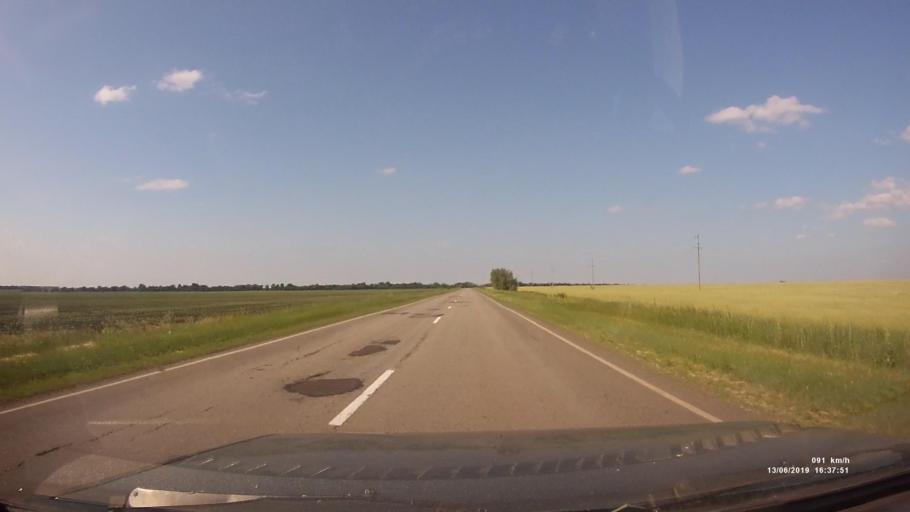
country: RU
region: Rostov
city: Kazanskaya
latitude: 49.9119
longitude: 41.3179
